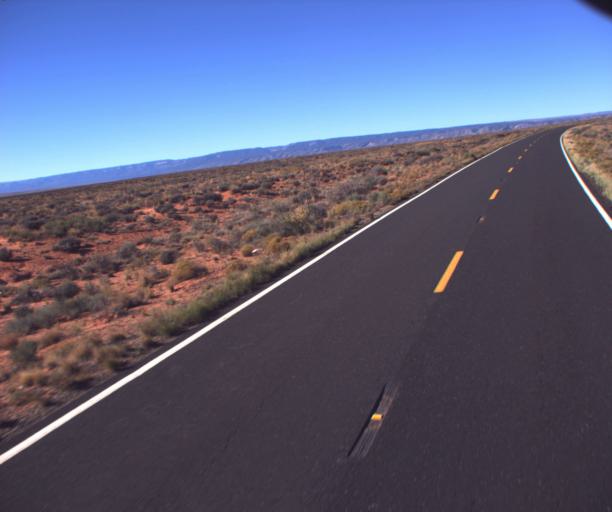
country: US
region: Arizona
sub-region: Coconino County
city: LeChee
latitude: 36.6883
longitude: -111.8235
